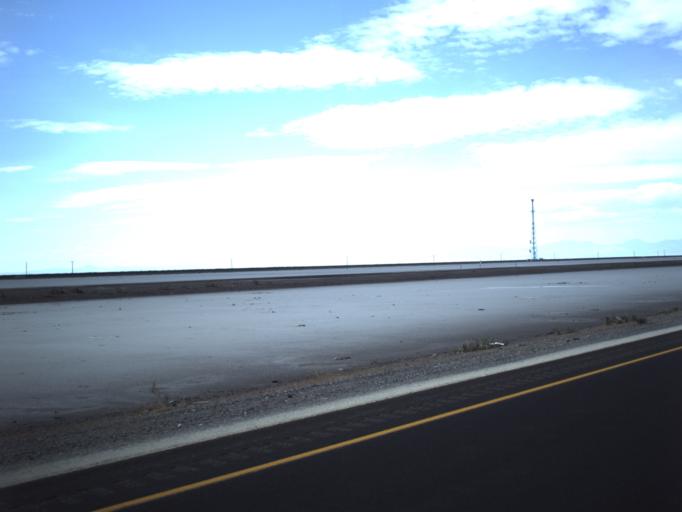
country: US
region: Utah
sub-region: Tooele County
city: Wendover
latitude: 40.7329
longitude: -113.5485
